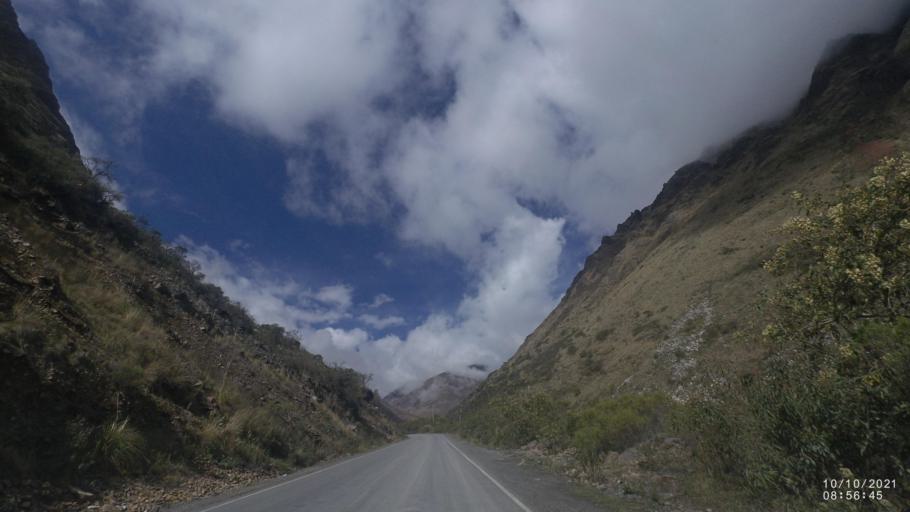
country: BO
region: La Paz
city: Quime
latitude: -16.9905
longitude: -67.2469
